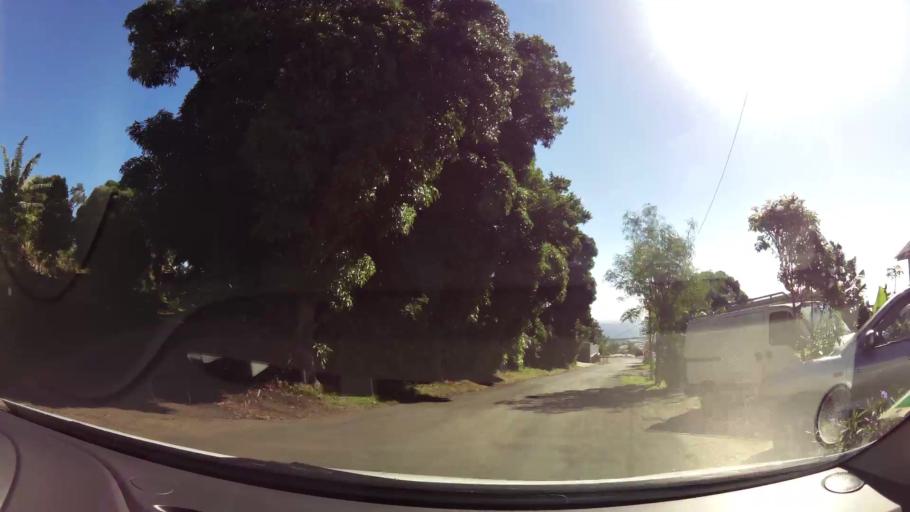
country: RE
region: Reunion
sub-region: Reunion
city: Saint-Denis
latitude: -20.9177
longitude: 55.4859
